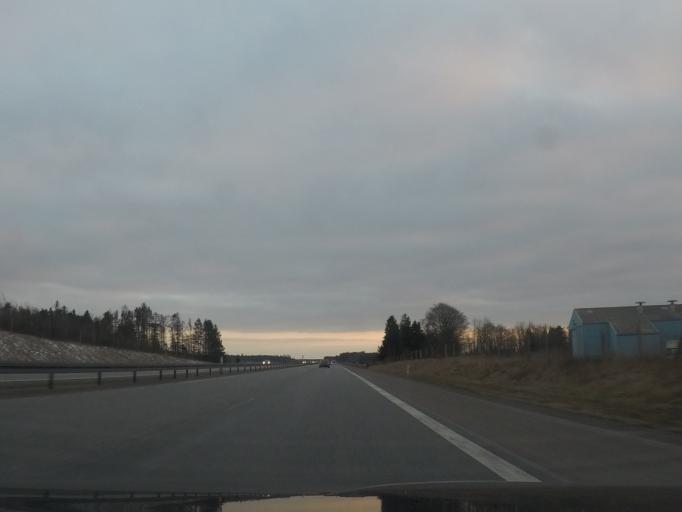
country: DK
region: Central Jutland
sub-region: Herning Kommune
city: Lind
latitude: 56.0644
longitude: 8.9972
